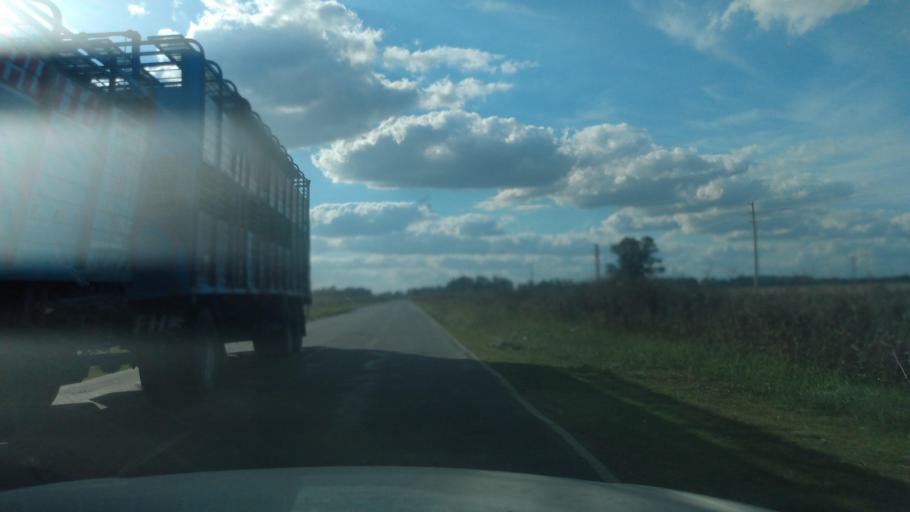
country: AR
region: Buenos Aires
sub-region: Partido de Mercedes
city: Mercedes
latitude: -34.7319
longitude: -59.3894
